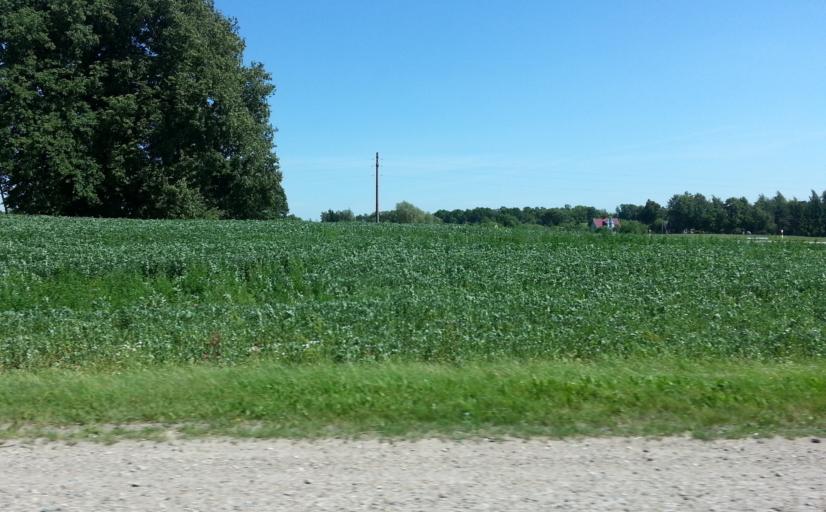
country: LT
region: Panevezys
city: Pasvalys
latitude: 56.0882
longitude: 24.4471
